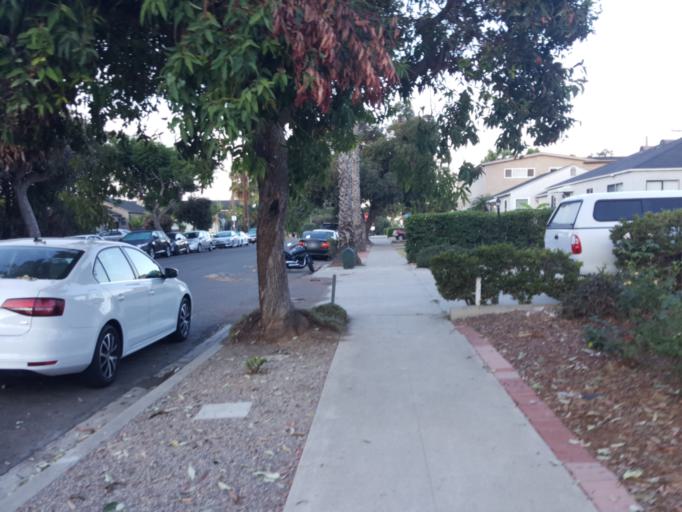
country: US
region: California
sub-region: San Diego County
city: La Jolla
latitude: 32.7988
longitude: -117.2414
